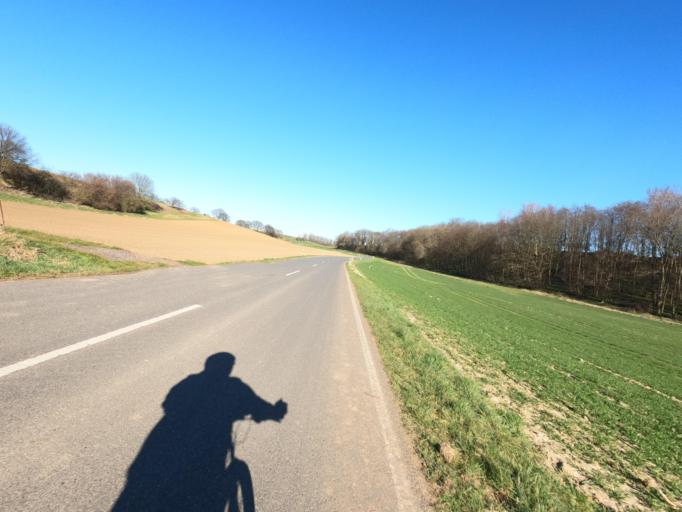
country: DE
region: North Rhine-Westphalia
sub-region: Regierungsbezirk Koln
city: Linnich
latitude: 50.9958
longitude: 6.2986
